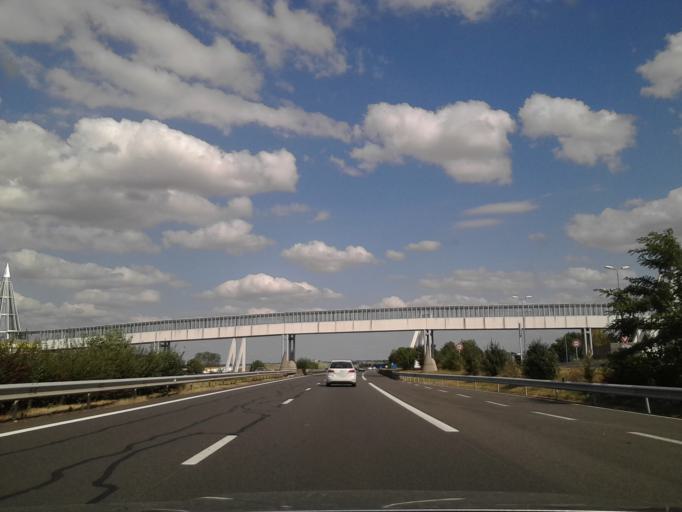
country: FR
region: Auvergne
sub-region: Departement de l'Allier
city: Doyet
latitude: 46.3562
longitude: 2.8009
